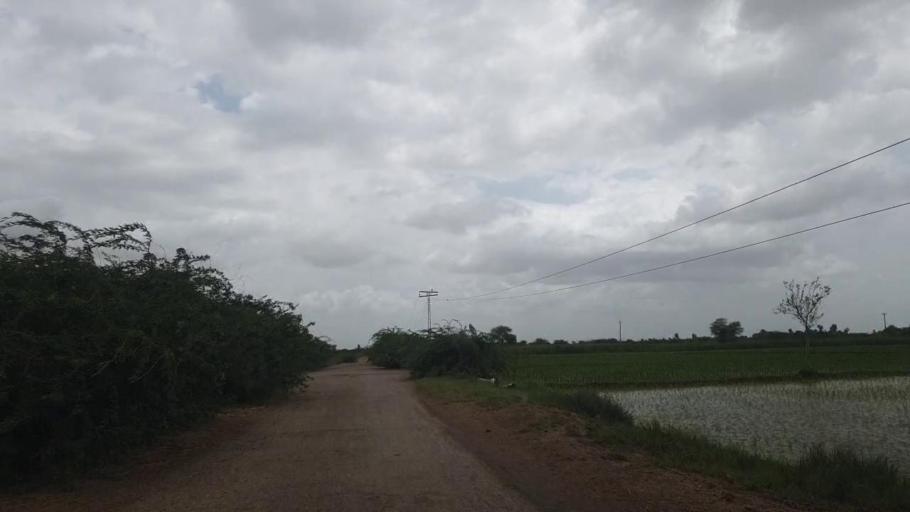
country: PK
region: Sindh
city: Badin
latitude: 24.6510
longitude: 68.9460
